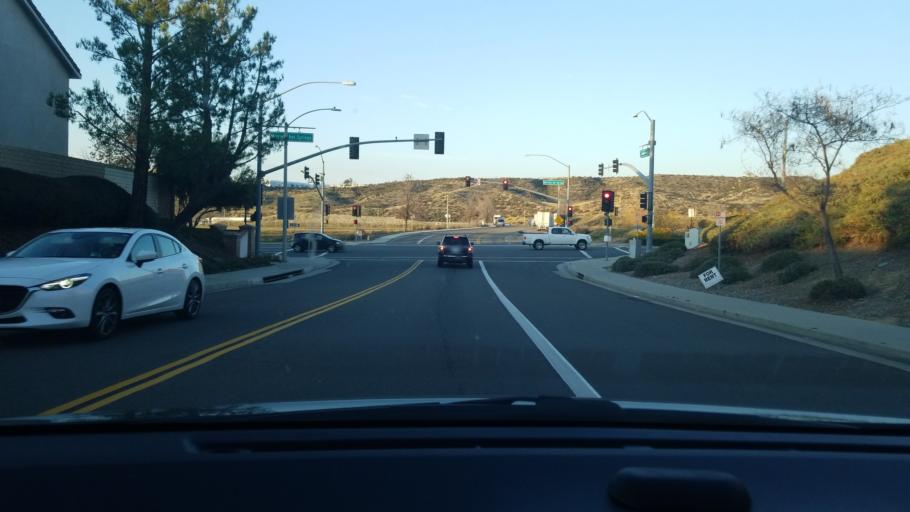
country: US
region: California
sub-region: Riverside County
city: Murrieta Hot Springs
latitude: 33.5517
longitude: -117.1323
